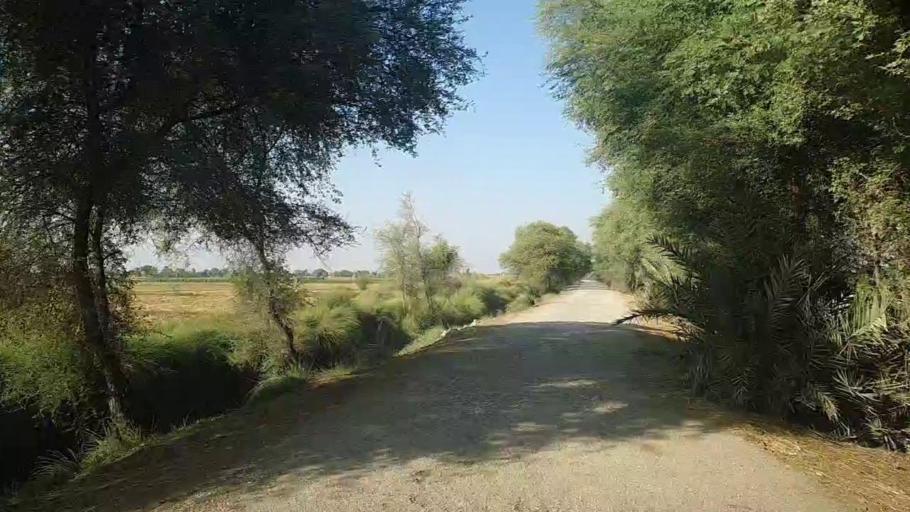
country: PK
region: Sindh
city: Tangwani
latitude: 28.2805
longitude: 68.9842
